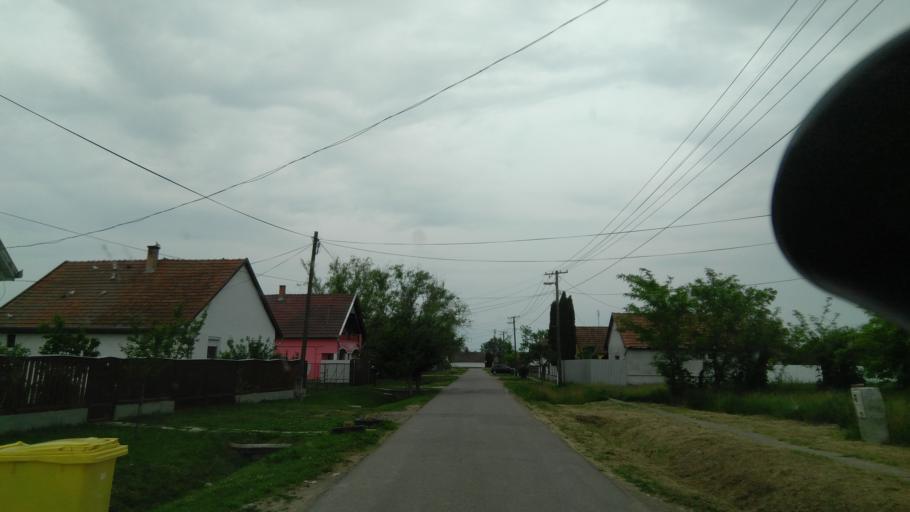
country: HU
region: Bekes
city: Doboz
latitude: 46.7318
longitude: 21.2506
